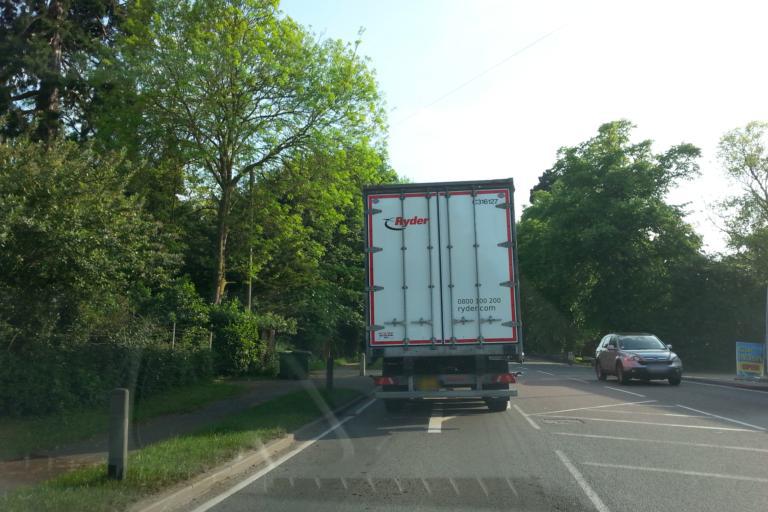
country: GB
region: England
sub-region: Cambridgeshire
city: Hemingford Grey
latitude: 52.3162
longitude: -0.0815
